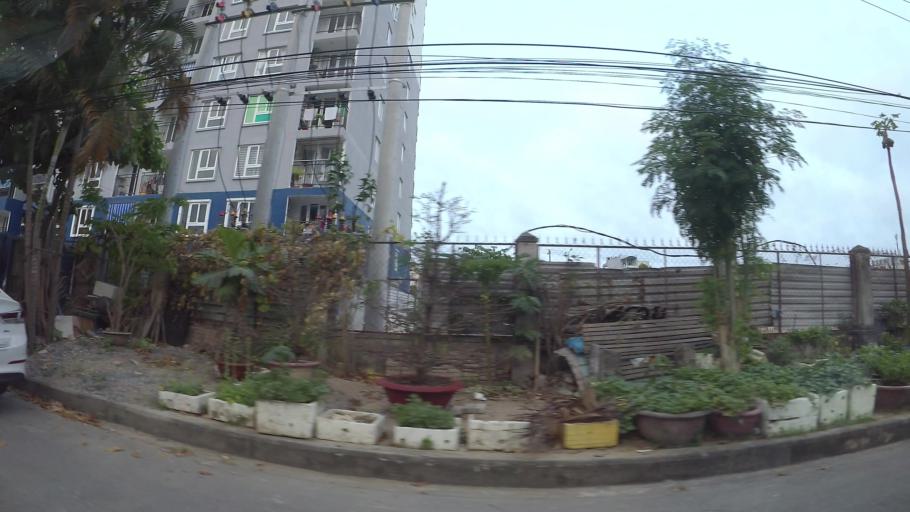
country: VN
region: Da Nang
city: Son Tra
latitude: 16.0560
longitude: 108.2353
